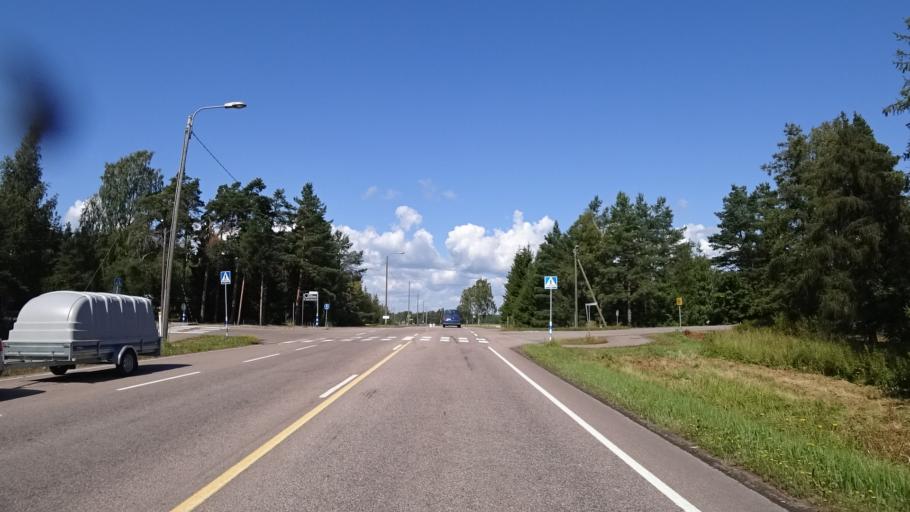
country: FI
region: Kymenlaakso
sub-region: Kotka-Hamina
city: Karhula
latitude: 60.5328
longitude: 26.9373
